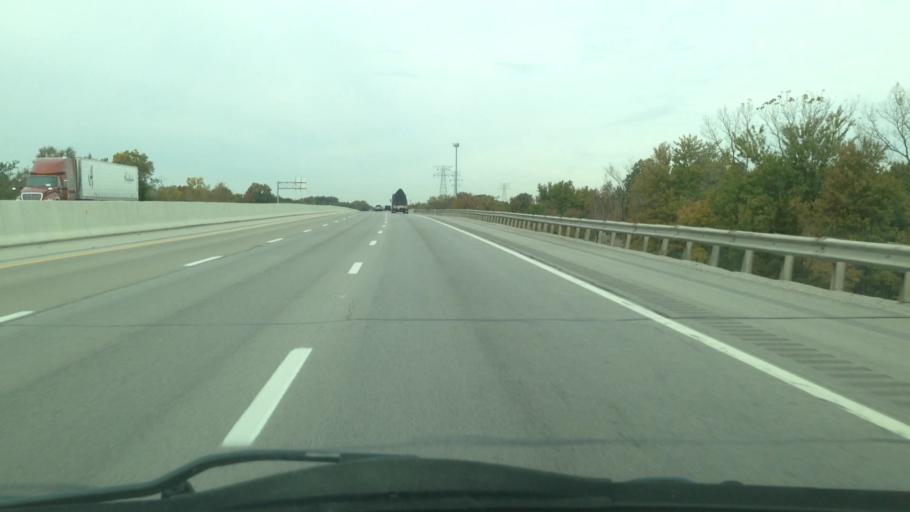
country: US
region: Ohio
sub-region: Wood County
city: Perrysburg
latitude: 41.5746
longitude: -83.5937
